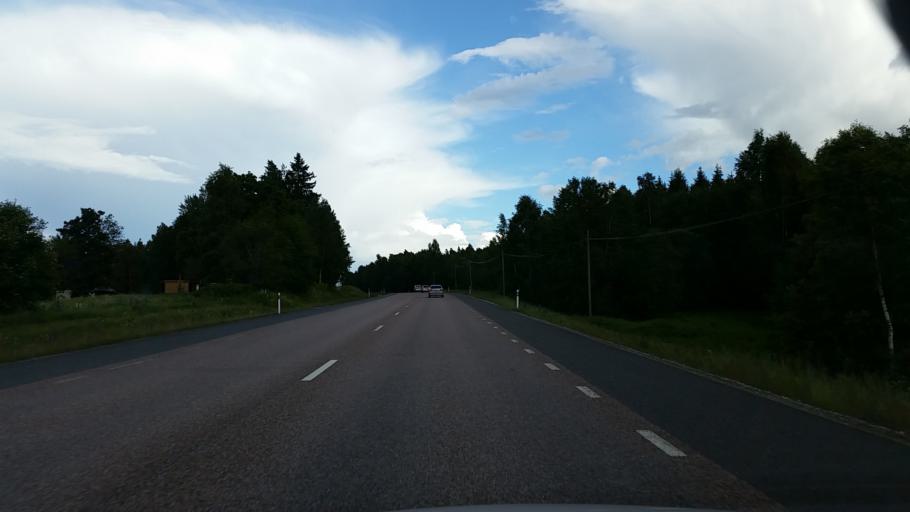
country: SE
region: Vaestmanland
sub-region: Fagersta Kommun
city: Fagersta
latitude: 59.9783
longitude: 15.6967
